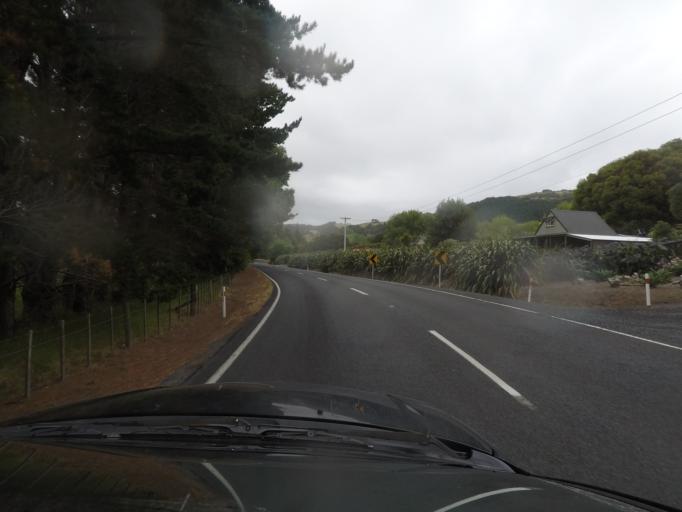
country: NZ
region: Auckland
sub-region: Auckland
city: Warkworth
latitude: -36.2666
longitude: 174.7008
